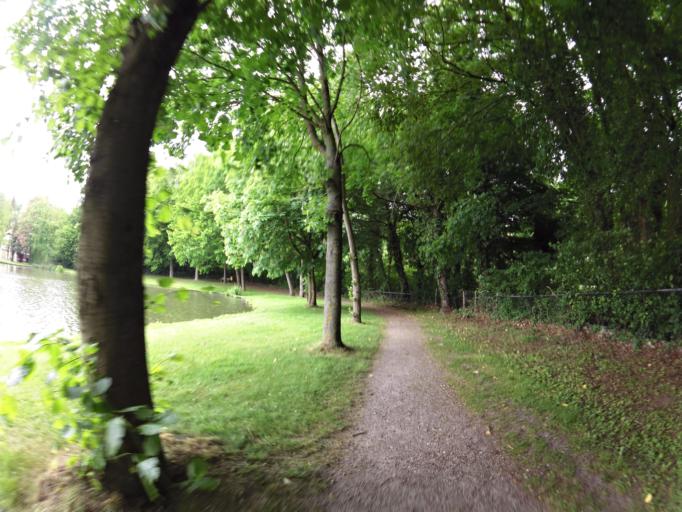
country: NL
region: Limburg
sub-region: Gemeente Kerkrade
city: Kerkrade
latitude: 50.8860
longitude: 6.0333
